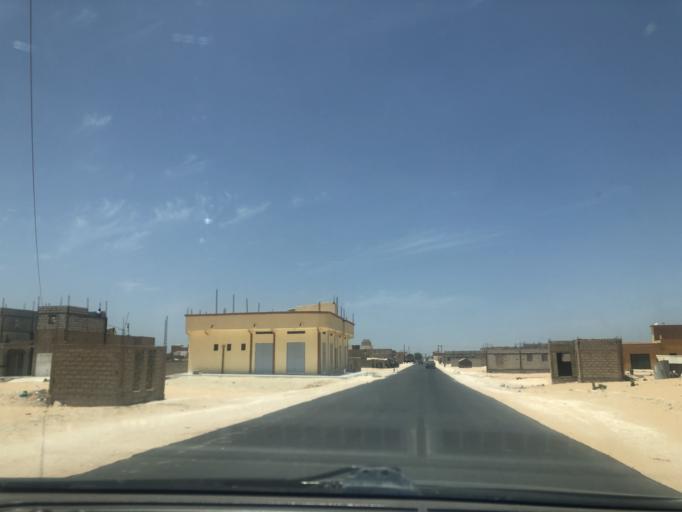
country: MR
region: Nouakchott
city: Nouakchott
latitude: 18.0035
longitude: -15.9618
